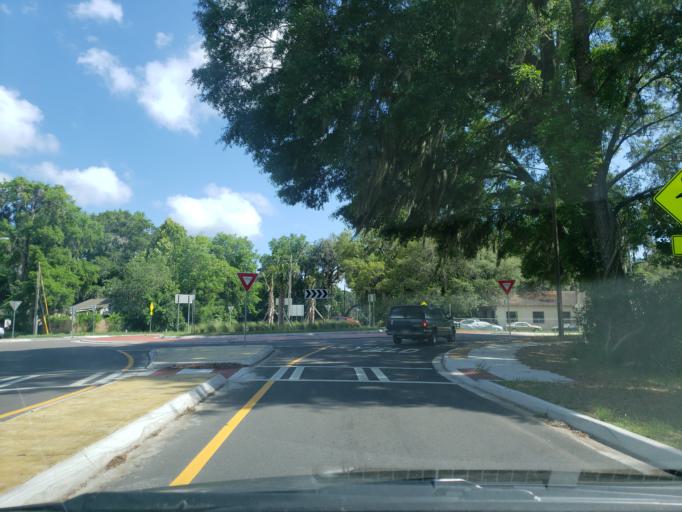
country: US
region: Georgia
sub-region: Chatham County
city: Thunderbolt
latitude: 32.0157
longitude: -81.0662
